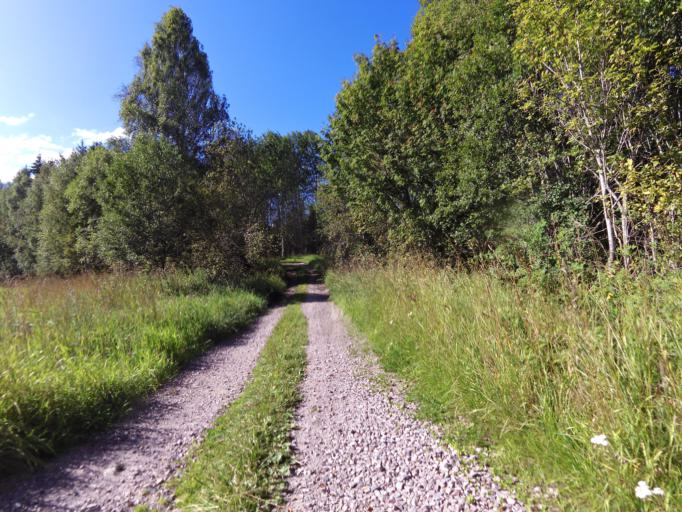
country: SE
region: Gaevleborg
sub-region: Hofors Kommun
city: Hofors
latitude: 60.5242
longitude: 16.4076
